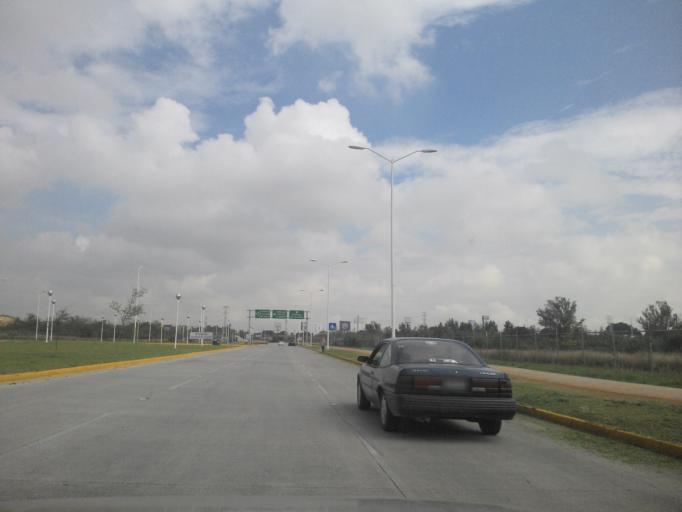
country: MX
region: Jalisco
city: Nuevo Mexico
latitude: 20.6934
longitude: -103.4615
